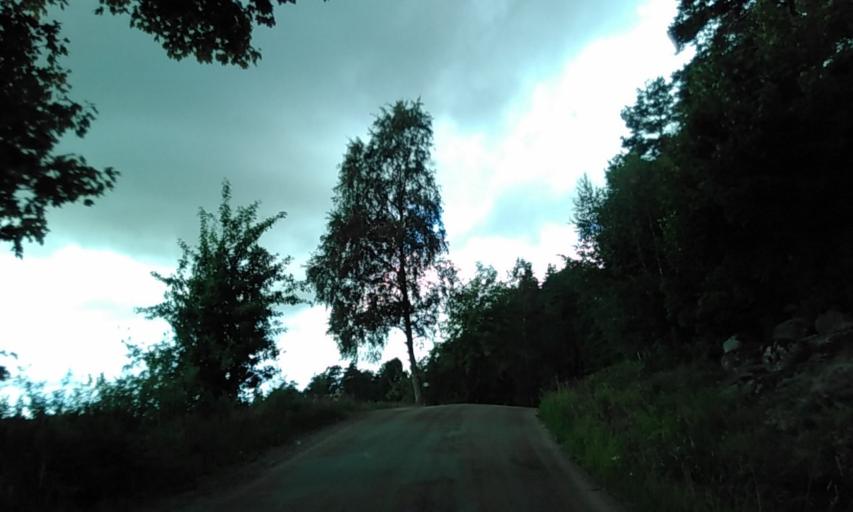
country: SE
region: Vaestra Goetaland
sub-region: Vargarda Kommun
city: Jonstorp
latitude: 57.9949
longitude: 12.6448
